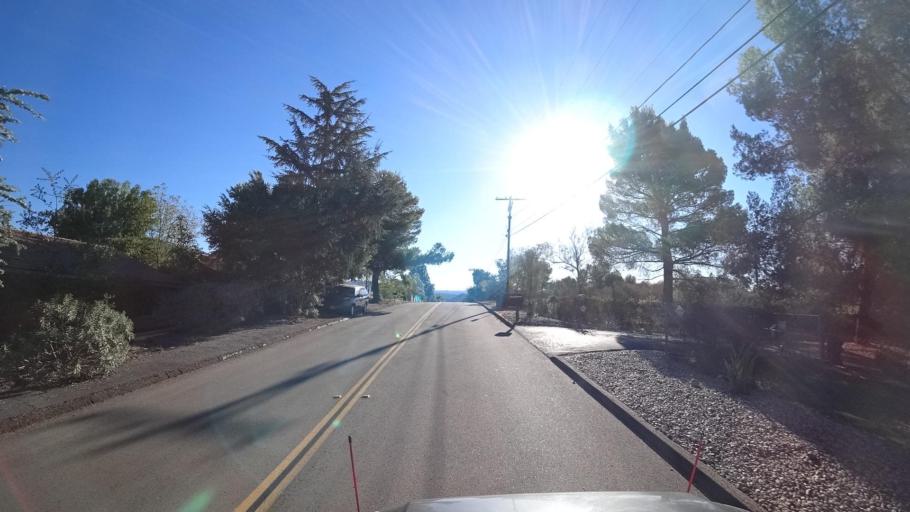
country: US
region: California
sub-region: San Diego County
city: Alpine
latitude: 32.8298
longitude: -116.7587
